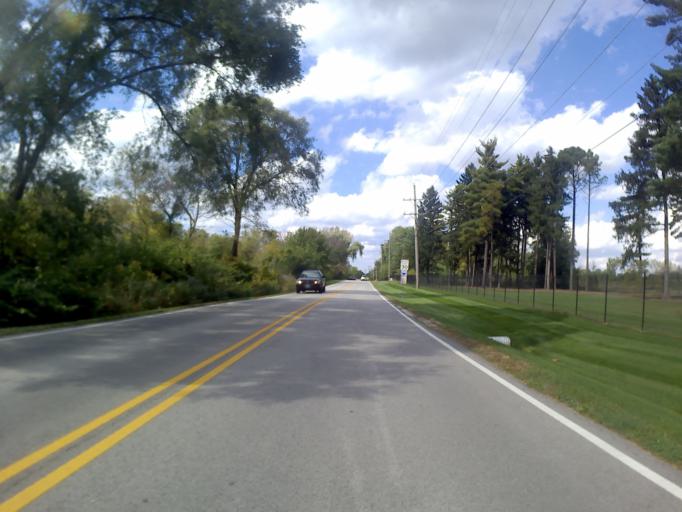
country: US
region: Illinois
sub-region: DuPage County
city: Lisle
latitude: 41.8188
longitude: -88.0960
